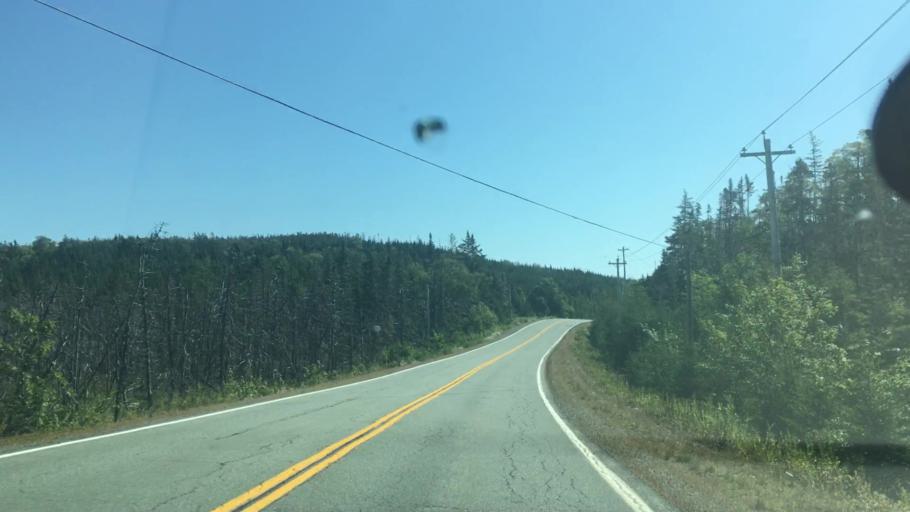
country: CA
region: Nova Scotia
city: Antigonish
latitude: 45.0123
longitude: -62.0940
